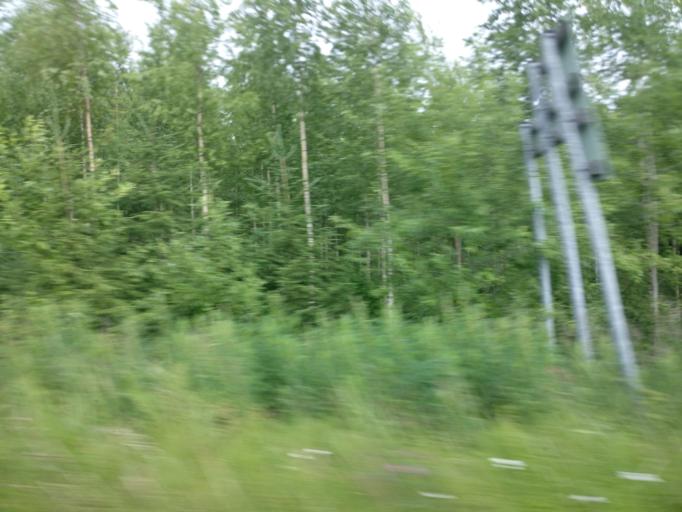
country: FI
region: Northern Savo
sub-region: Koillis-Savo
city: Juankoski
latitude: 62.9959
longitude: 28.2523
